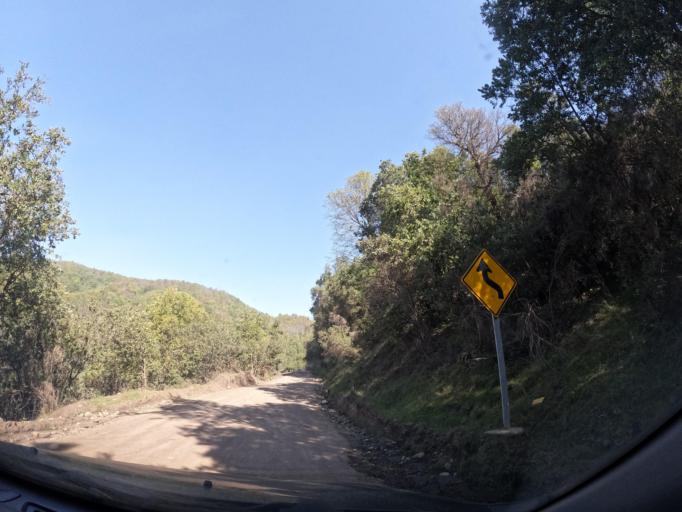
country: CL
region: Maule
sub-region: Provincia de Linares
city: Longavi
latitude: -36.2402
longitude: -71.4407
